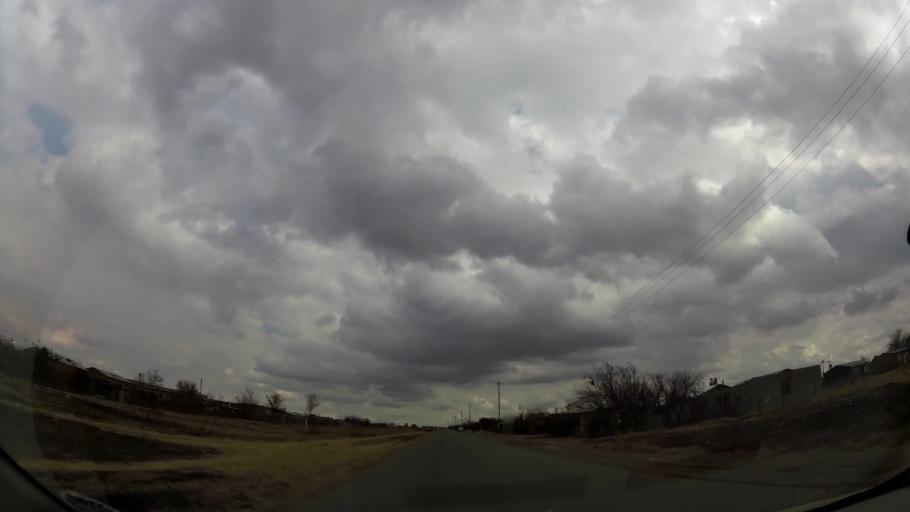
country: ZA
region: Orange Free State
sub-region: Fezile Dabi District Municipality
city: Sasolburg
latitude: -26.8507
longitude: 27.8744
